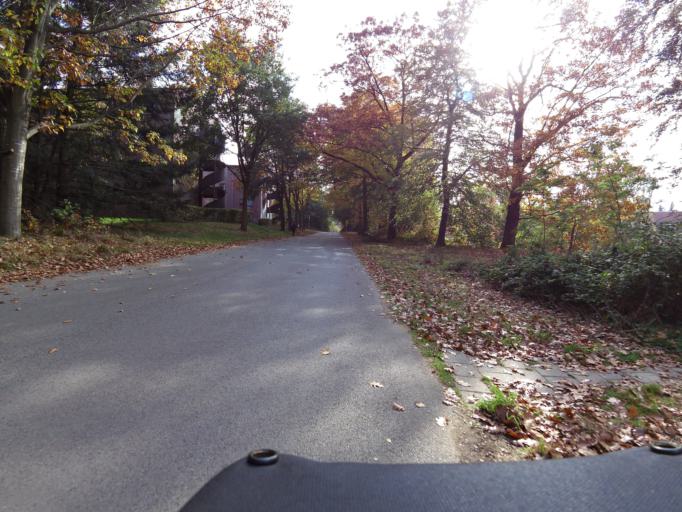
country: NL
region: Gelderland
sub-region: Gemeente Ede
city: Ede
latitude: 52.0309
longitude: 5.6756
